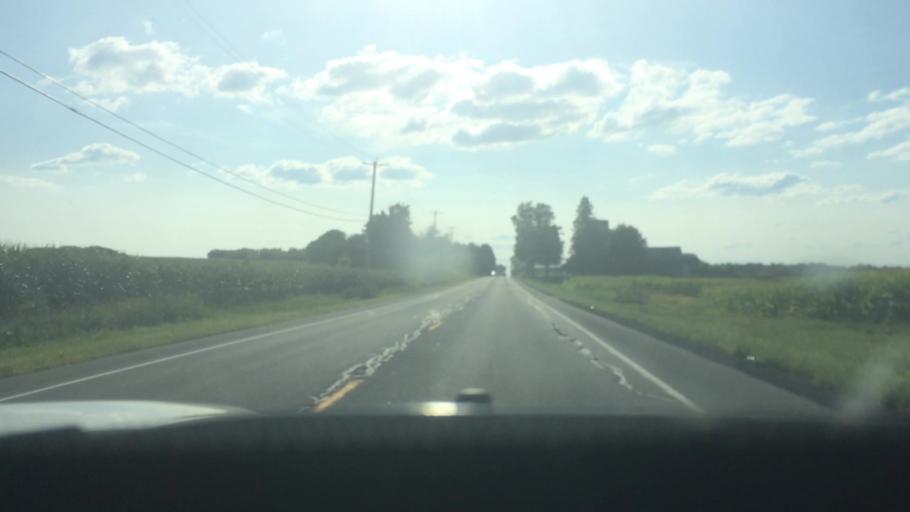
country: US
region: New York
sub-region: St. Lawrence County
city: Hannawa Falls
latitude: 44.6918
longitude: -74.6837
